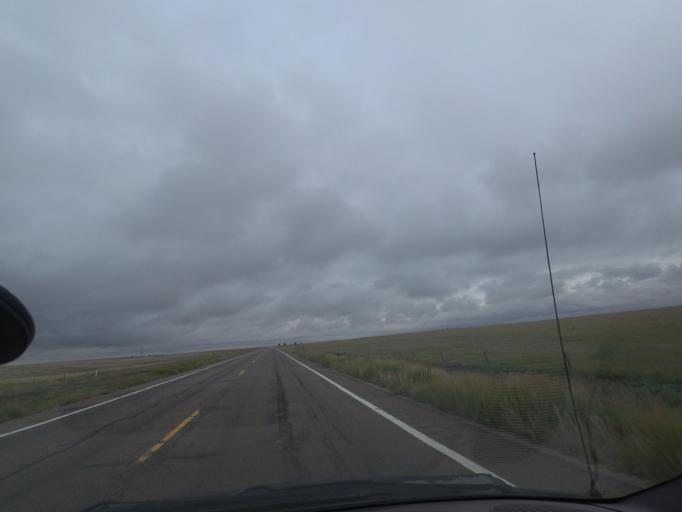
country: US
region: Colorado
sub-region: Yuma County
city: Yuma
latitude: 39.6773
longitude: -102.9618
